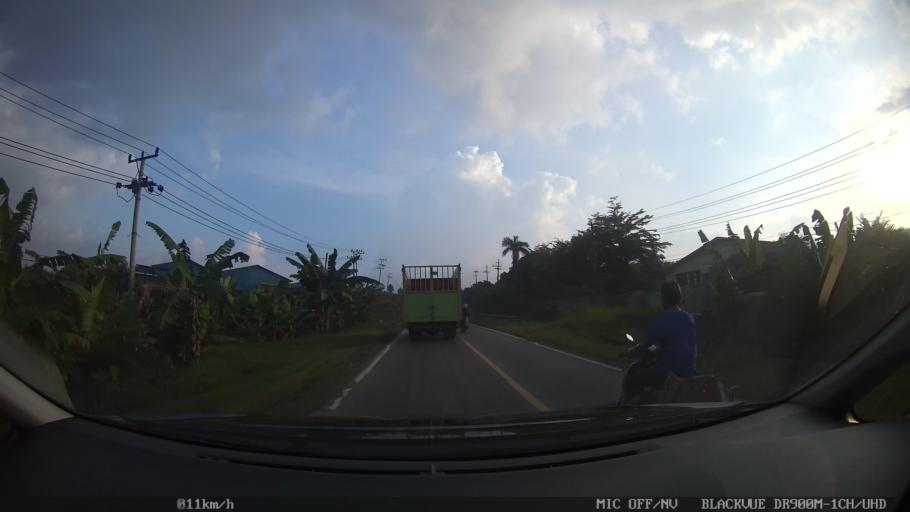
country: ID
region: Lampung
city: Panjang
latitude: -5.4051
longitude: 105.3499
